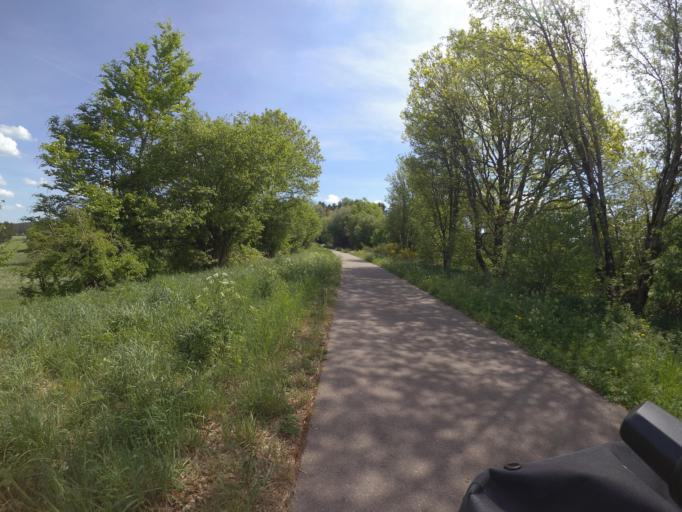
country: BE
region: Wallonia
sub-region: Province de Liege
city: Bullange
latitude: 50.3802
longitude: 6.2916
